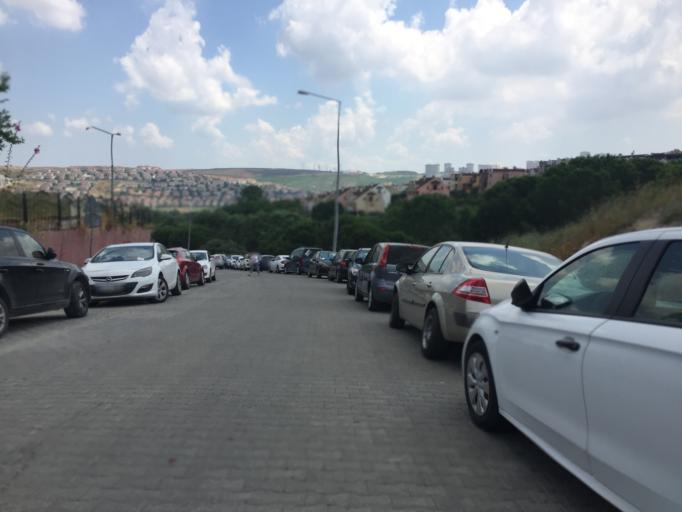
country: TR
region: Istanbul
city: Esenyurt
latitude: 41.0806
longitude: 28.6633
